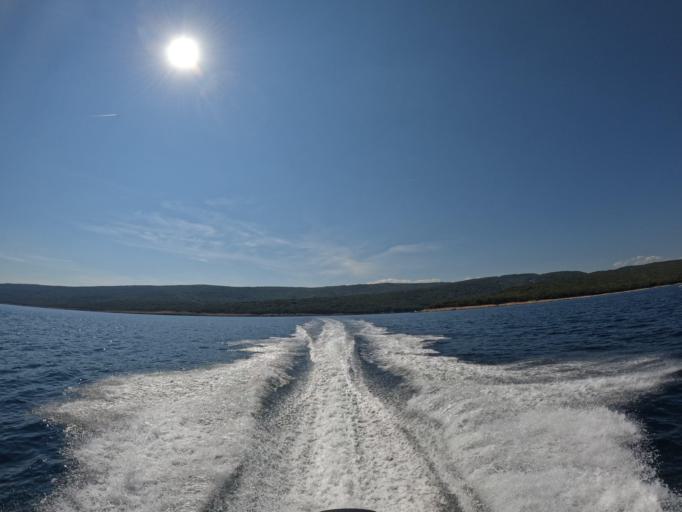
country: HR
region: Primorsko-Goranska
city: Cres
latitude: 44.9461
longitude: 14.4764
